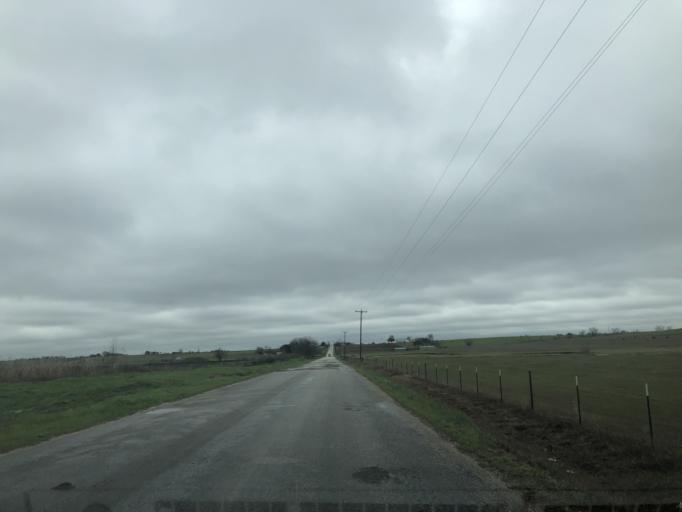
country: US
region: Texas
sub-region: Williamson County
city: Hutto
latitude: 30.5885
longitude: -97.4994
